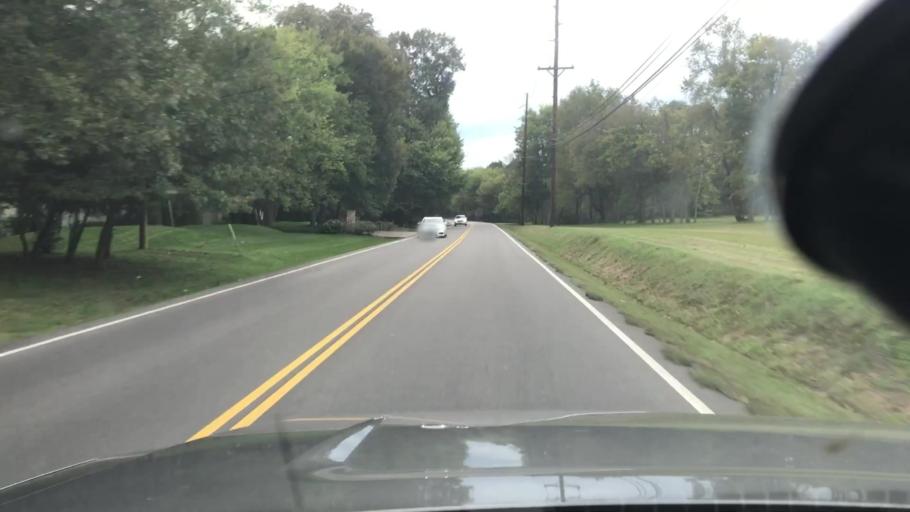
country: US
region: Tennessee
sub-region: Davidson County
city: Forest Hills
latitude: 36.0495
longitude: -86.8706
